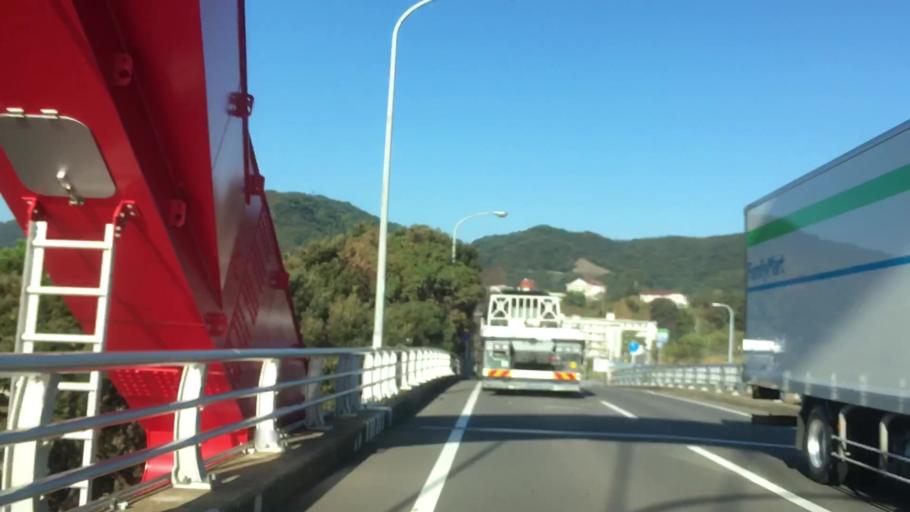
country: JP
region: Nagasaki
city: Sasebo
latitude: 33.0370
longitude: 129.6274
